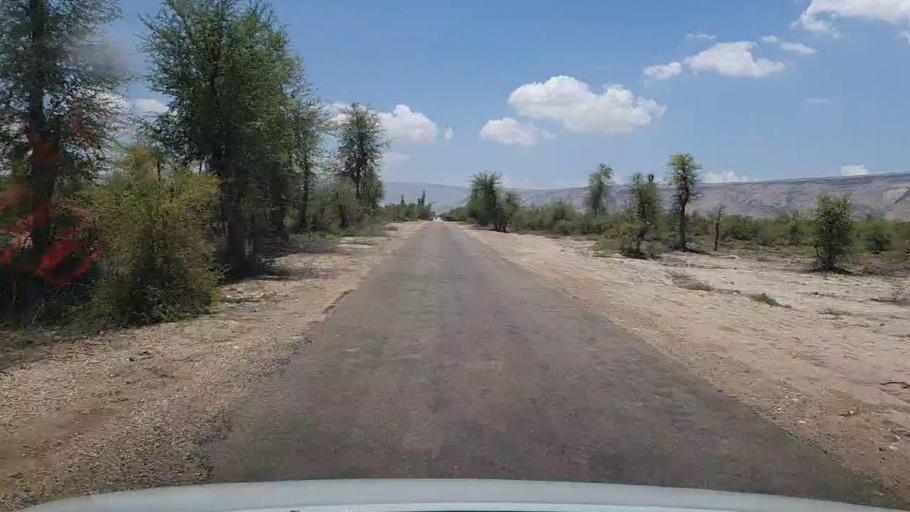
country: PK
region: Sindh
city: Bhan
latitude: 26.2805
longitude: 67.5293
